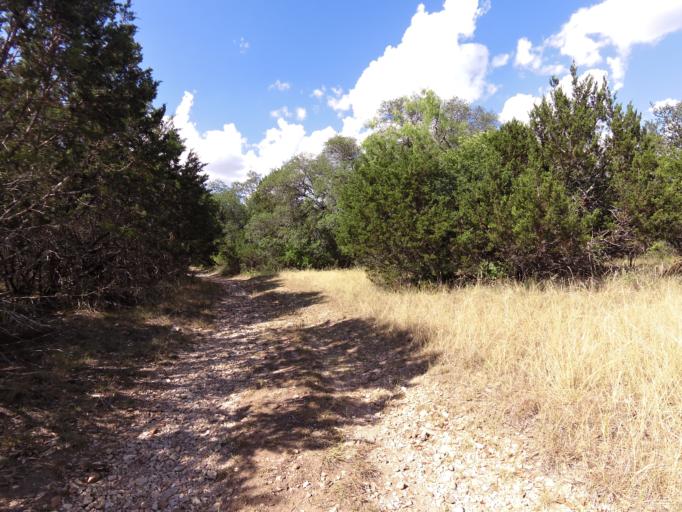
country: US
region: Texas
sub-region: Bexar County
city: Helotes
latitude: 29.5802
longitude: -98.6303
